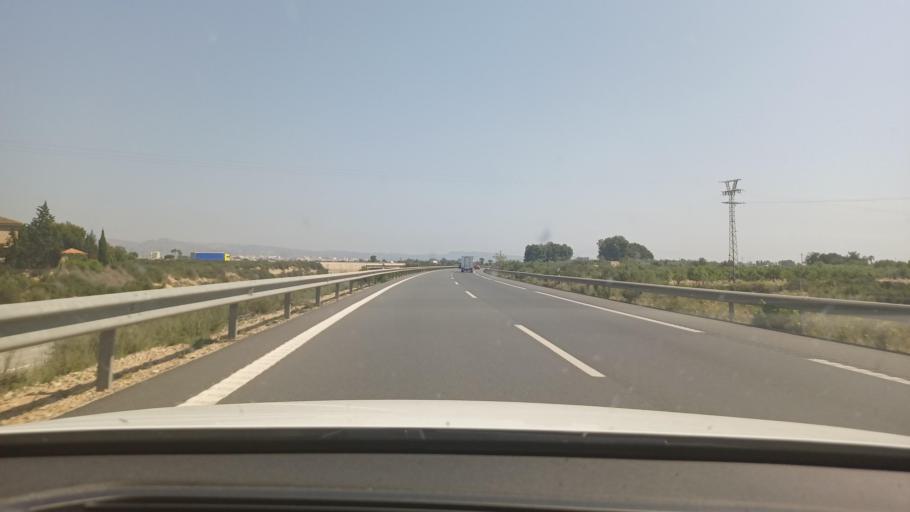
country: ES
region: Valencia
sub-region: Provincia de Alicante
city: Crevillente
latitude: 38.2151
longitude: -0.8162
